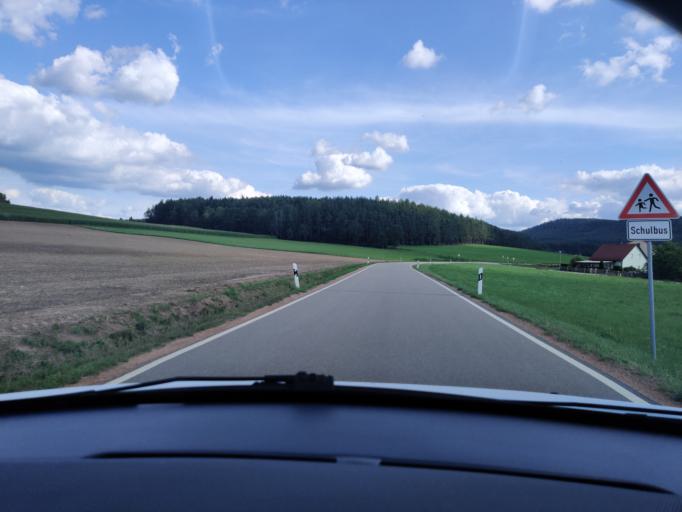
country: DE
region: Bavaria
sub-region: Upper Palatinate
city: Nabburg
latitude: 49.4396
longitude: 12.1913
